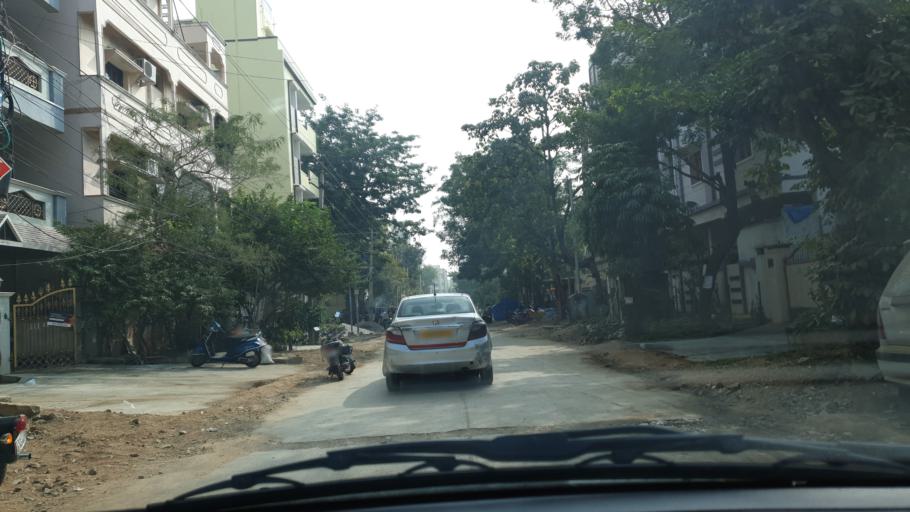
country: IN
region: Telangana
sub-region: Rangareddi
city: Kukatpalli
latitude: 17.4849
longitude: 78.4060
